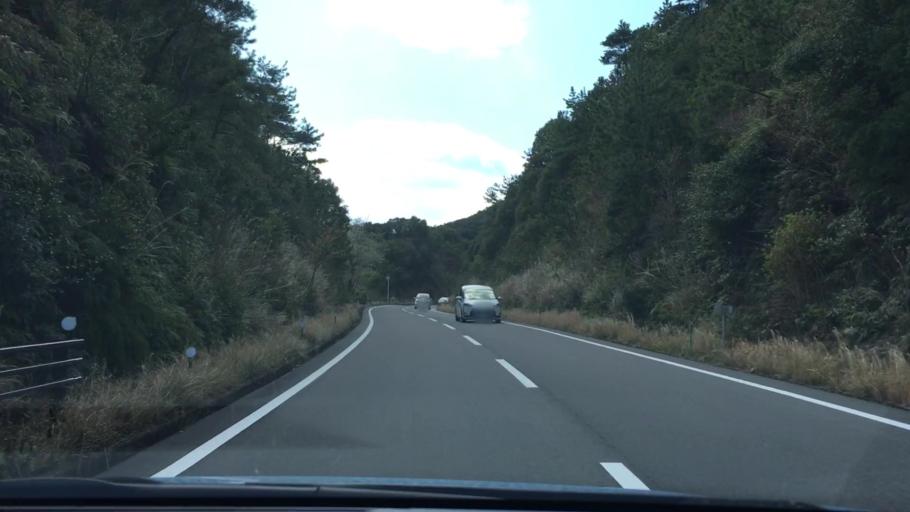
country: JP
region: Mie
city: Toba
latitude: 34.4340
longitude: 136.9125
